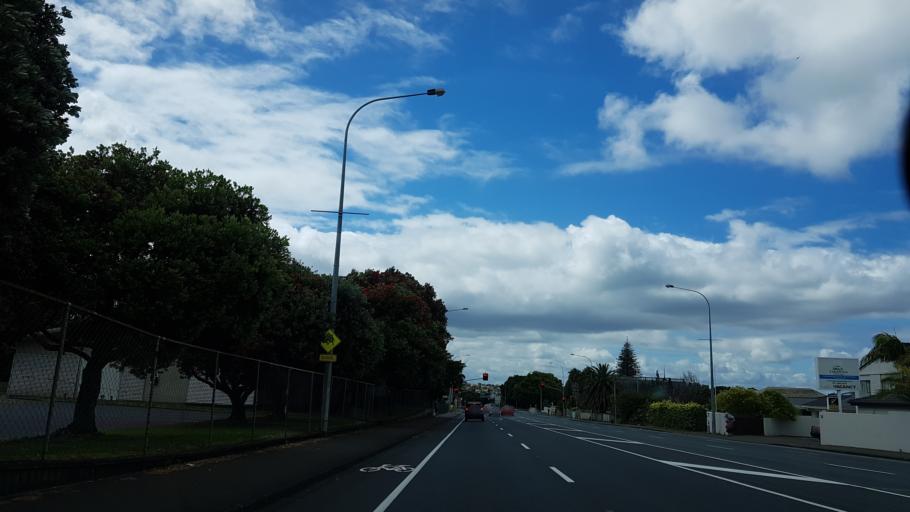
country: NZ
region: Auckland
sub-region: Auckland
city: North Shore
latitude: -36.7883
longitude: 174.7599
